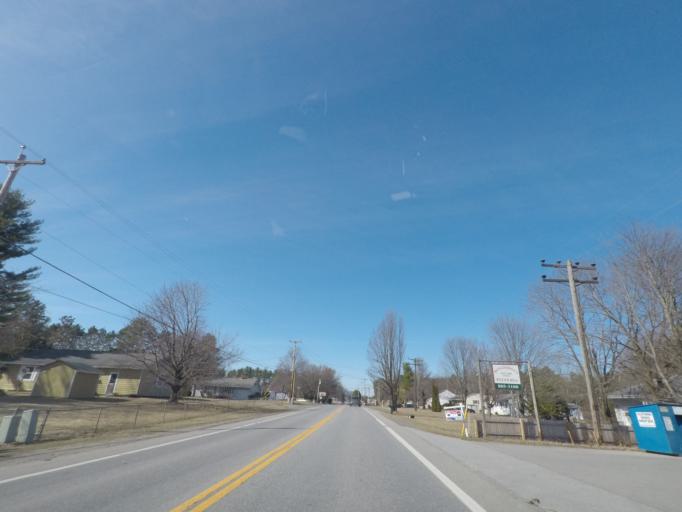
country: US
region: New York
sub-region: Saratoga County
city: Milton
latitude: 43.0401
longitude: -73.8496
